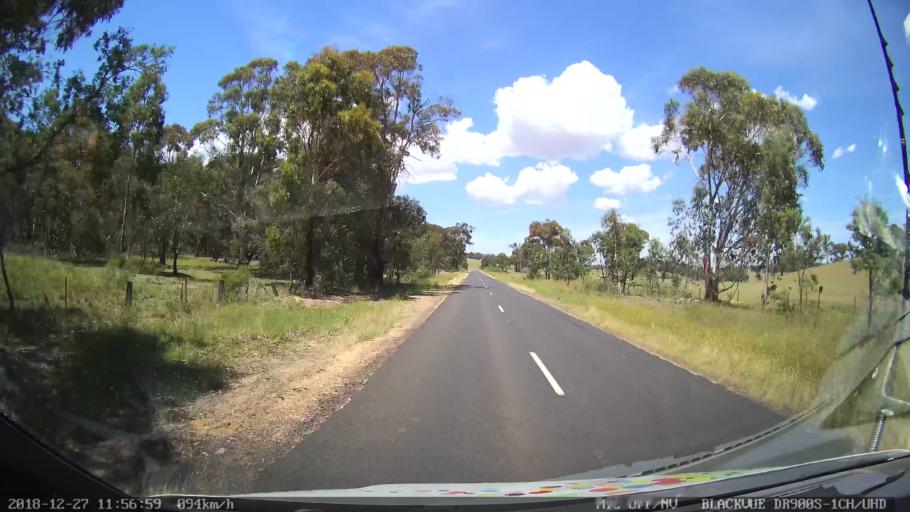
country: AU
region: New South Wales
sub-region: Blayney
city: Blayney
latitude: -33.7053
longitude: 149.3873
